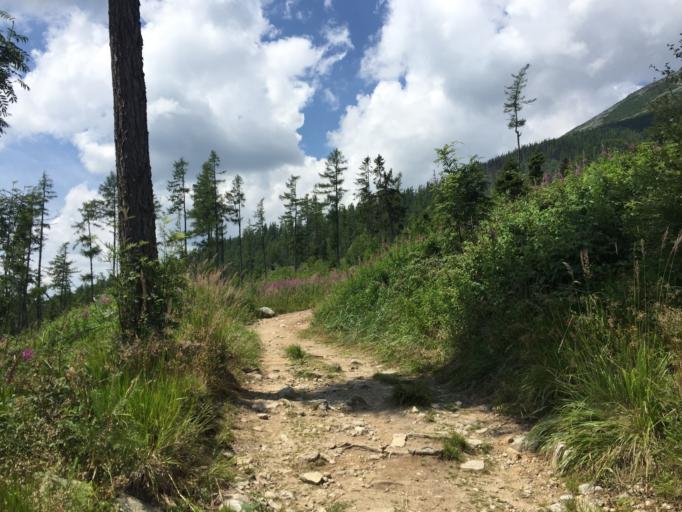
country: SK
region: Presovsky
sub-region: Okres Poprad
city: Vysoke Tatry
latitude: 49.1497
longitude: 20.2087
